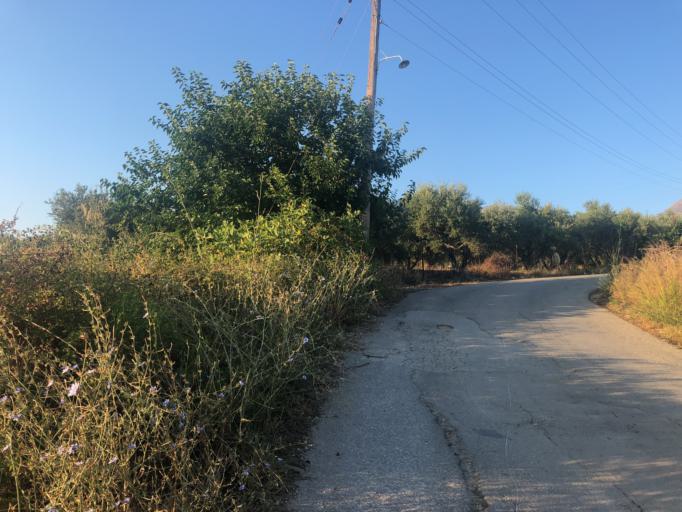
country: GR
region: Crete
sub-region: Nomos Chanias
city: Georgioupolis
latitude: 35.3430
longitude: 24.3013
